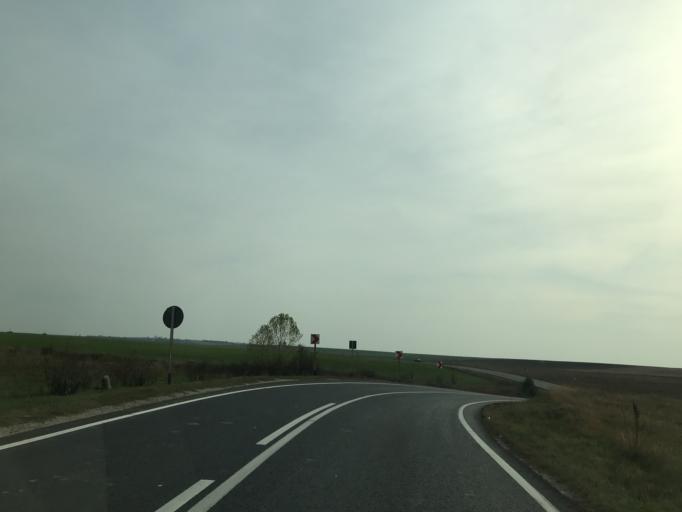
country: RO
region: Olt
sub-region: Comuna Piatra Olt
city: Piatra
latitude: 44.3415
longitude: 24.2955
